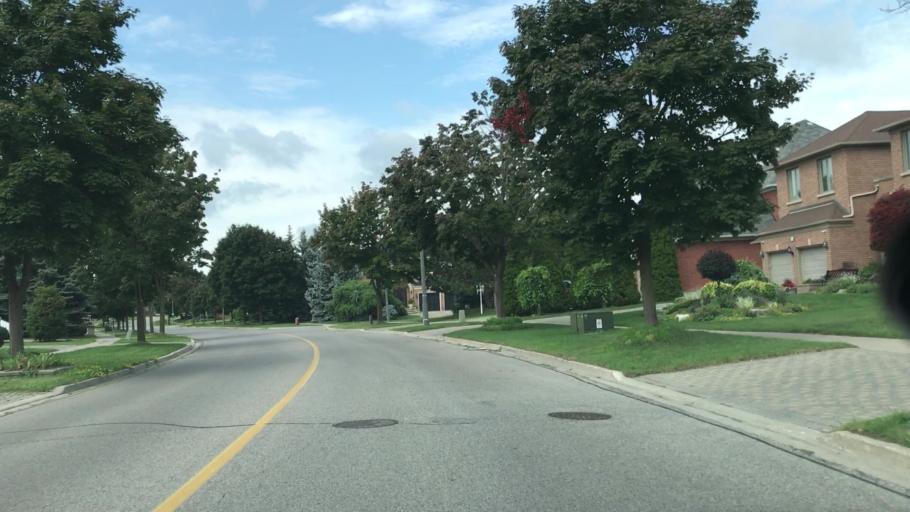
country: CA
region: Ontario
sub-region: York
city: Richmond Hill
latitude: 43.8651
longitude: -79.3972
